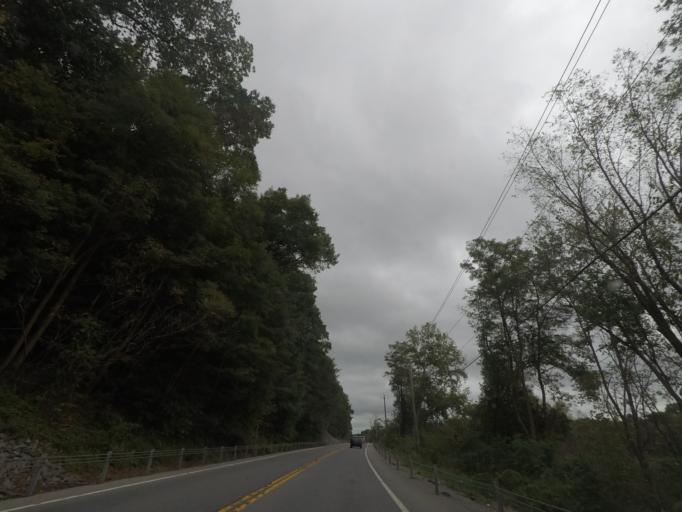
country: US
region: New York
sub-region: Saratoga County
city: Mechanicville
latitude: 42.9235
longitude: -73.7362
